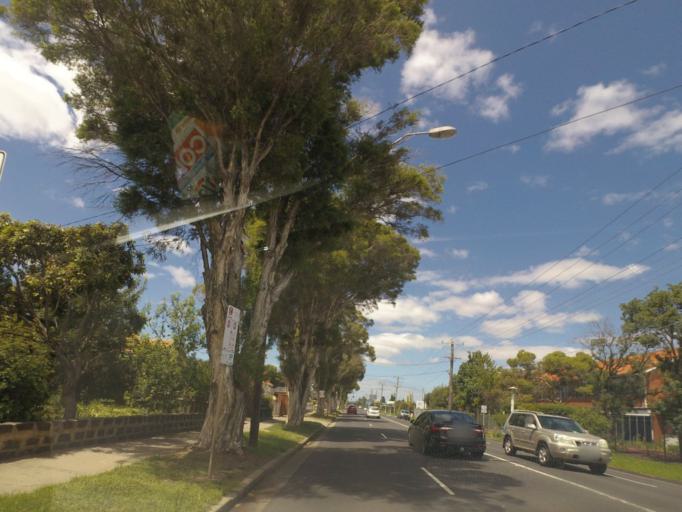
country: AU
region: Victoria
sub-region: Brimbank
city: Sunshine North
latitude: -37.7698
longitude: 144.8301
